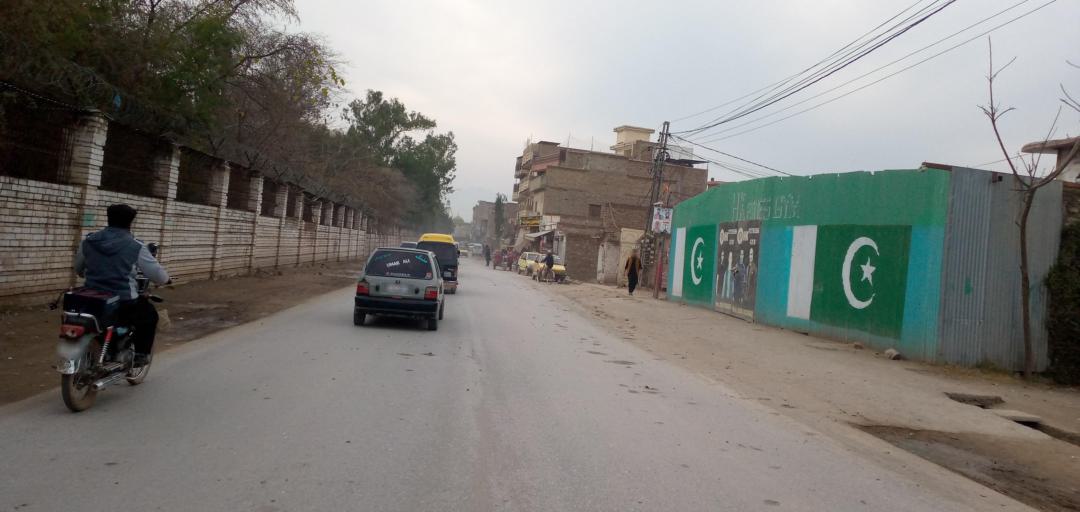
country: PK
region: Khyber Pakhtunkhwa
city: Peshawar
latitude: 34.0231
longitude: 71.4893
